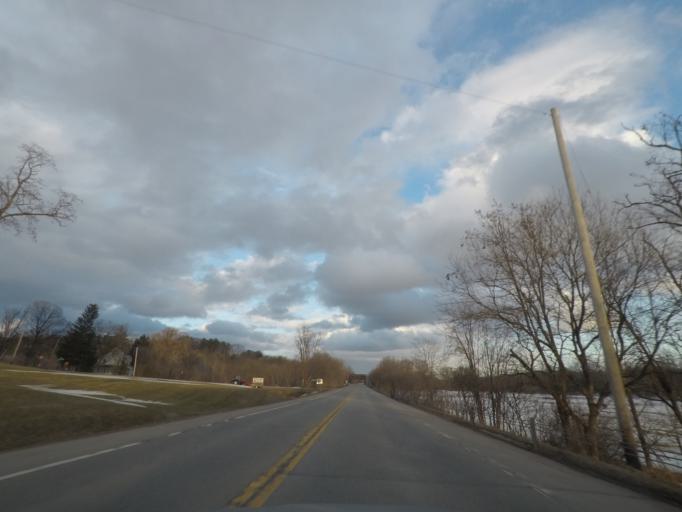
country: US
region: New York
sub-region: Montgomery County
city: Saint Johnsville
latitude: 43.0063
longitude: -74.7450
